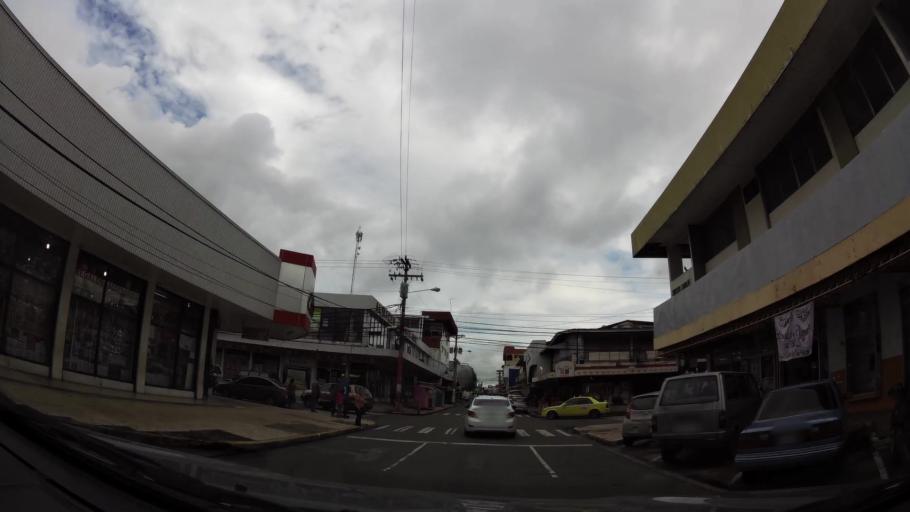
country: PA
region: Chiriqui
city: David
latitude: 8.4267
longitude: -82.4261
